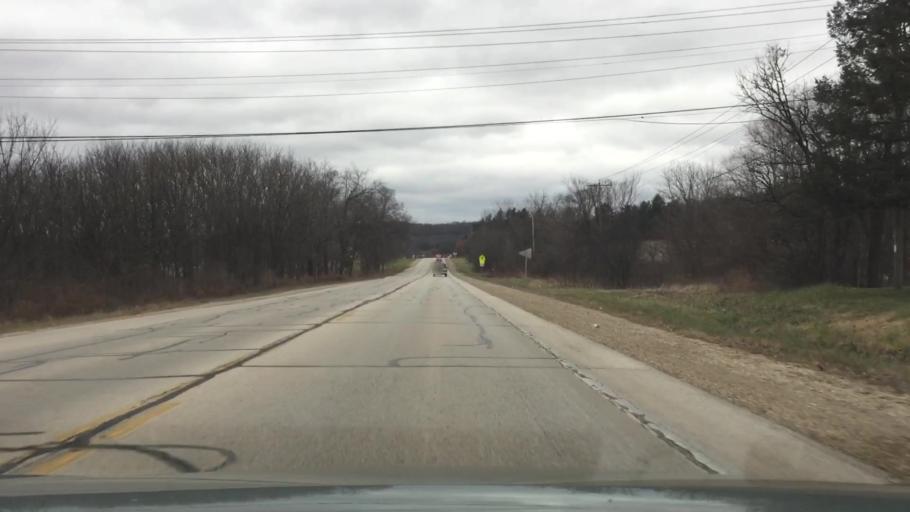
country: US
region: Wisconsin
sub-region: Waukesha County
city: Waukesha
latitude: 43.0210
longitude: -88.2755
